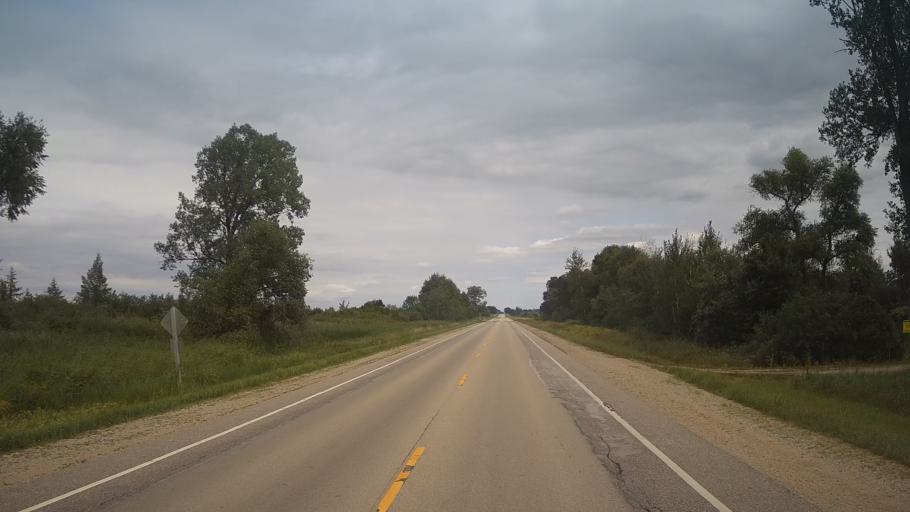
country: US
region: Wisconsin
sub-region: Green Lake County
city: Berlin
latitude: 44.0487
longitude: -88.9660
